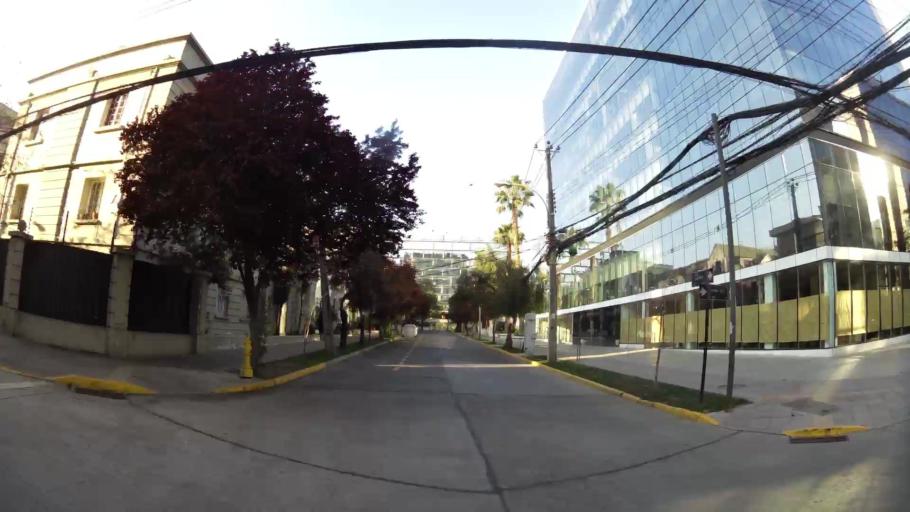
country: CL
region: Santiago Metropolitan
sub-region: Provincia de Santiago
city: Santiago
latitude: -33.4246
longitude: -70.6192
